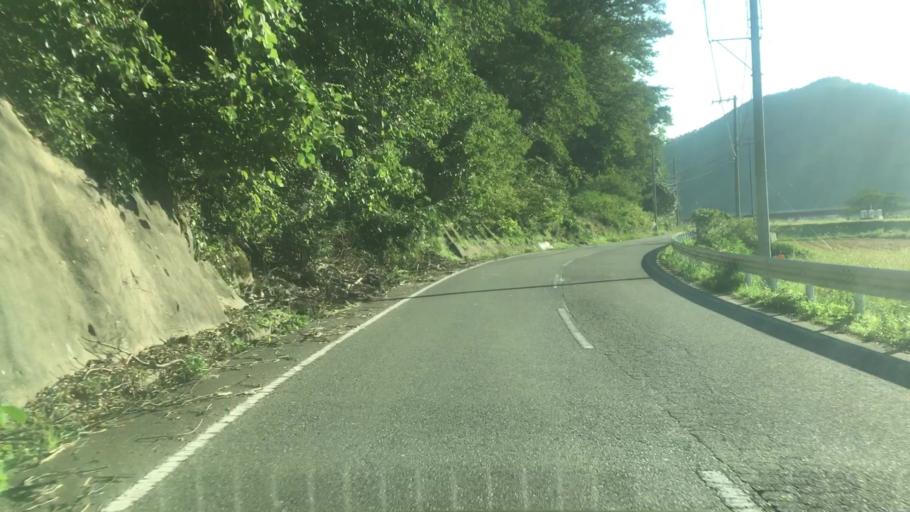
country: JP
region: Hyogo
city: Toyooka
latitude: 35.6094
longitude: 134.8085
